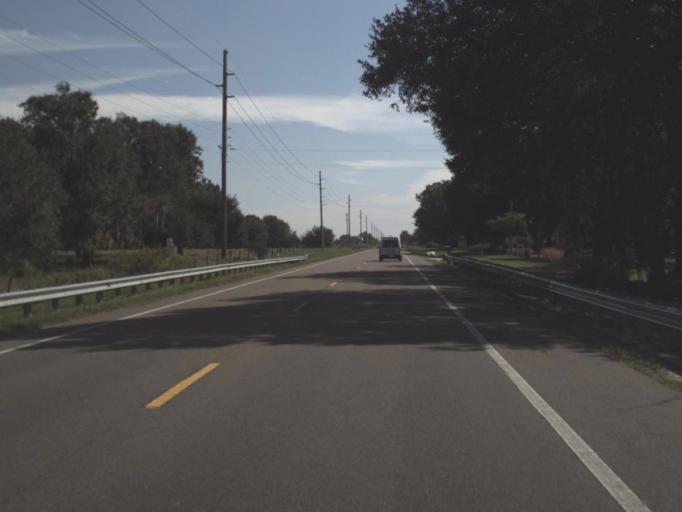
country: US
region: Florida
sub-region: Hardee County
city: Wauchula
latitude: 27.5514
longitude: -81.7473
